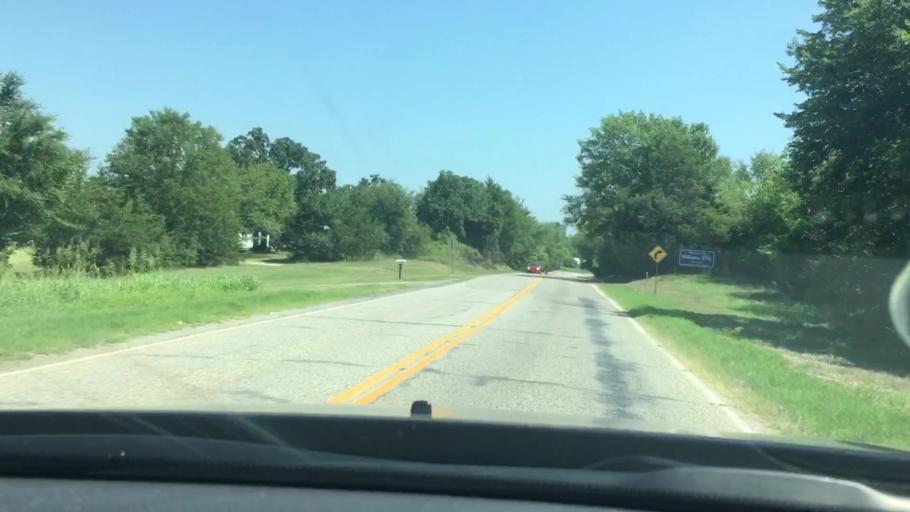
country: US
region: Oklahoma
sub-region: Johnston County
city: Tishomingo
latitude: 34.2386
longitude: -96.5582
